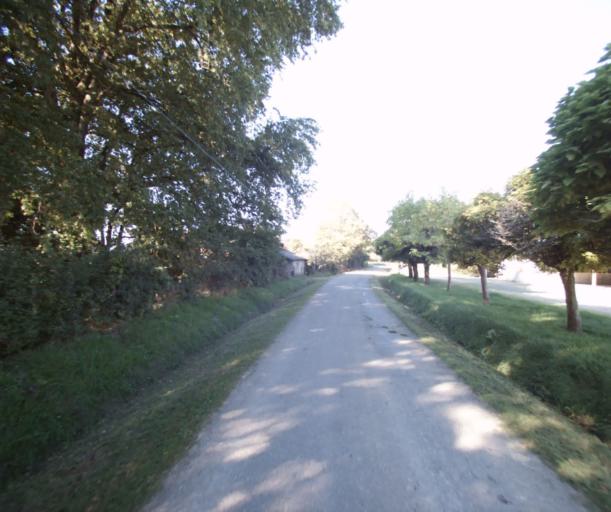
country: FR
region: Aquitaine
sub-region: Departement des Landes
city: Gabarret
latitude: 43.9063
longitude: 0.0124
